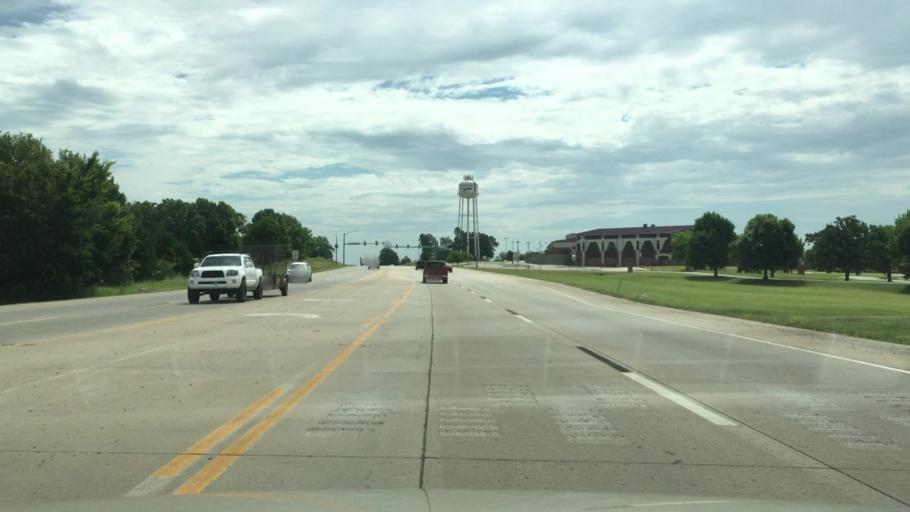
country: US
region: Oklahoma
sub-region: Cherokee County
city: Park Hill
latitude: 35.8493
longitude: -95.0062
